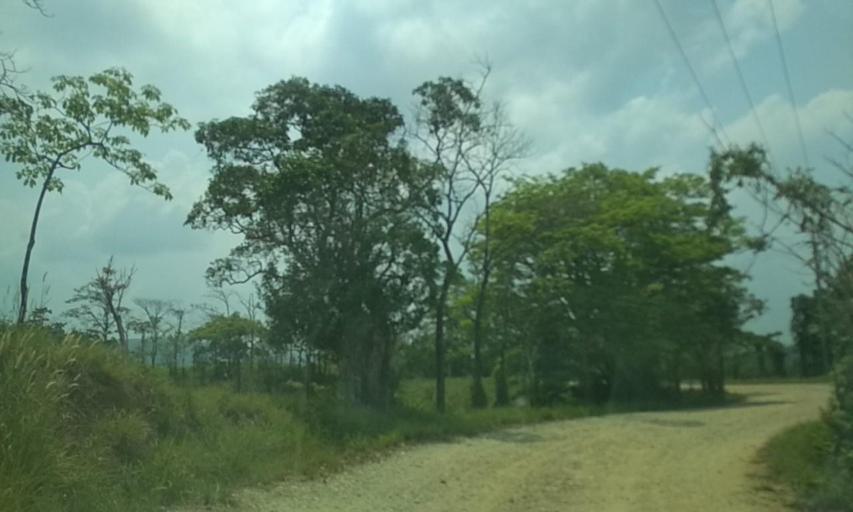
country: MX
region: Tabasco
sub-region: Huimanguillo
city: Francisco Rueda
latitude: 17.6123
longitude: -93.8118
